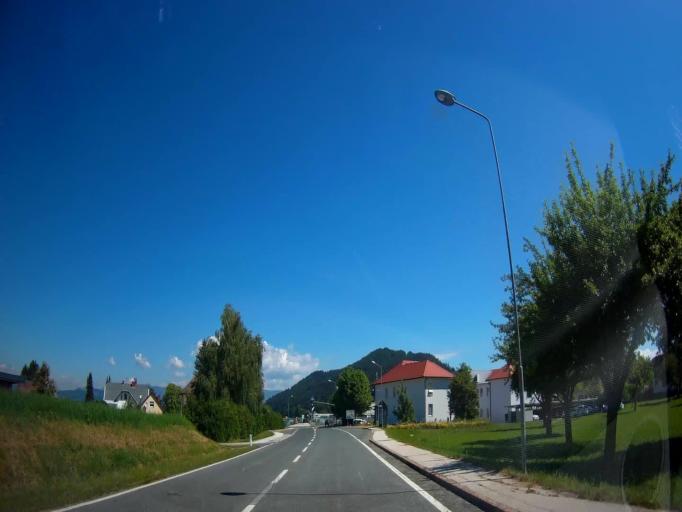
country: AT
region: Carinthia
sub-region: Politischer Bezirk Volkermarkt
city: Eberndorf
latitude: 46.5884
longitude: 14.6357
